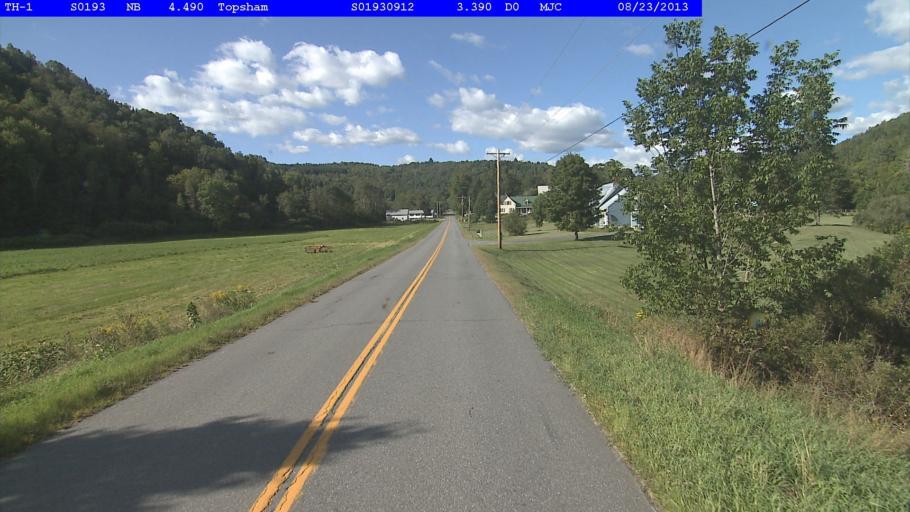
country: US
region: New Hampshire
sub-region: Grafton County
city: Haverhill
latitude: 44.1161
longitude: -72.2330
